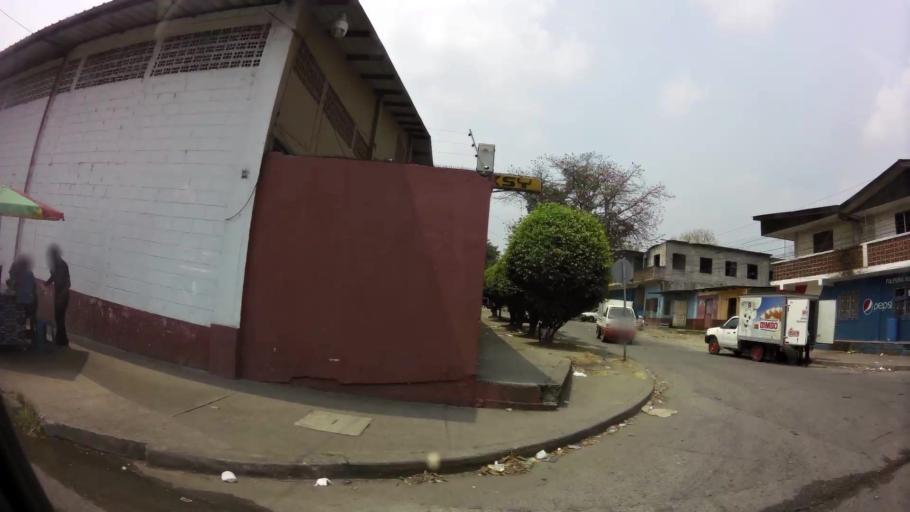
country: HN
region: Cortes
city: San Pedro Sula
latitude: 15.4839
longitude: -88.0285
